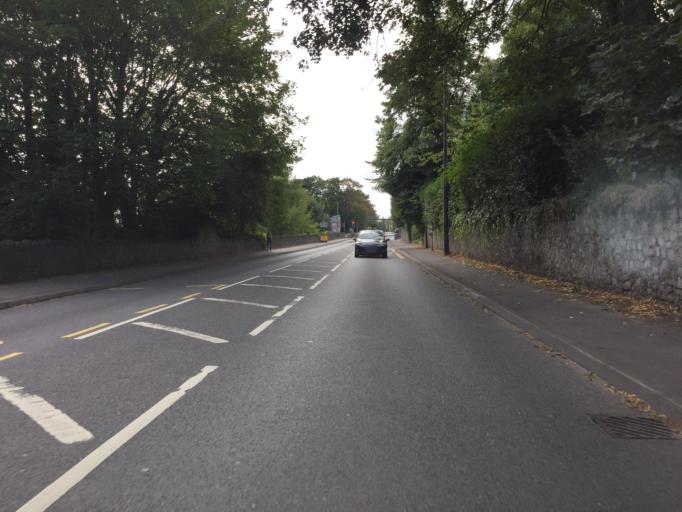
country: GB
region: England
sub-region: Kent
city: Maidstone
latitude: 51.2793
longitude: 0.5069
